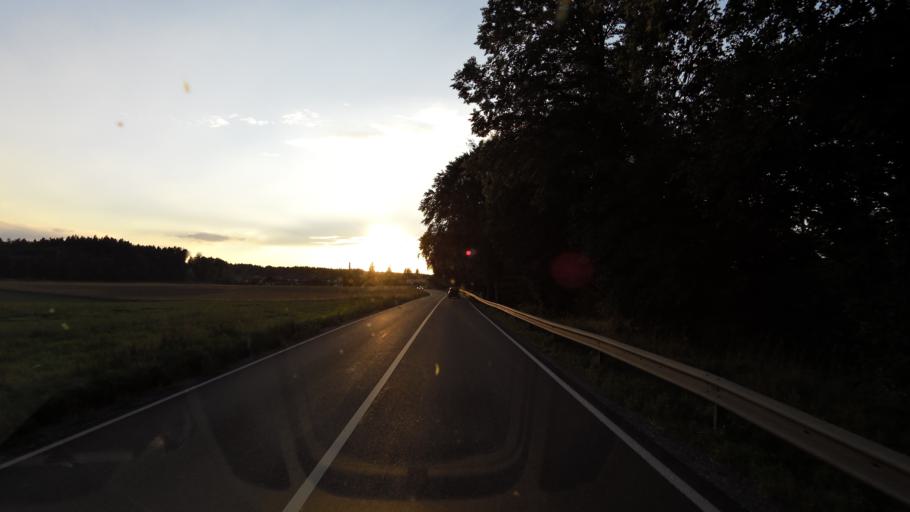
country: DE
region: Bavaria
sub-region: Upper Bavaria
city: Traunreut
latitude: 47.9436
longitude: 12.5856
